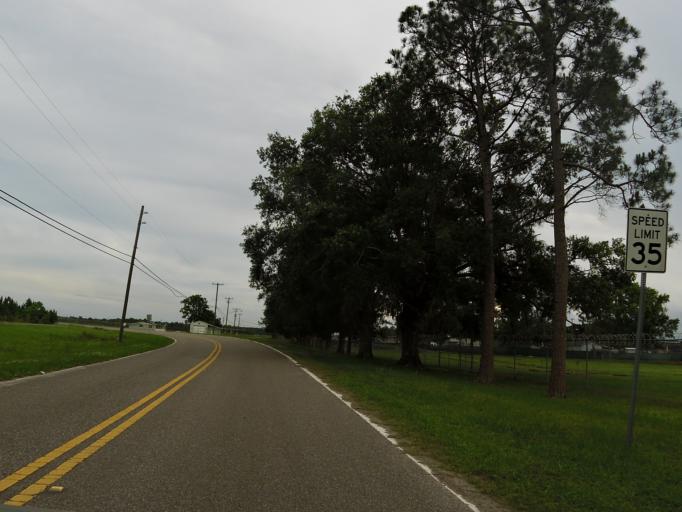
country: US
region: Florida
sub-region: Nassau County
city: Nassau Village-Ratliff
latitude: 30.5474
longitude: -81.7291
